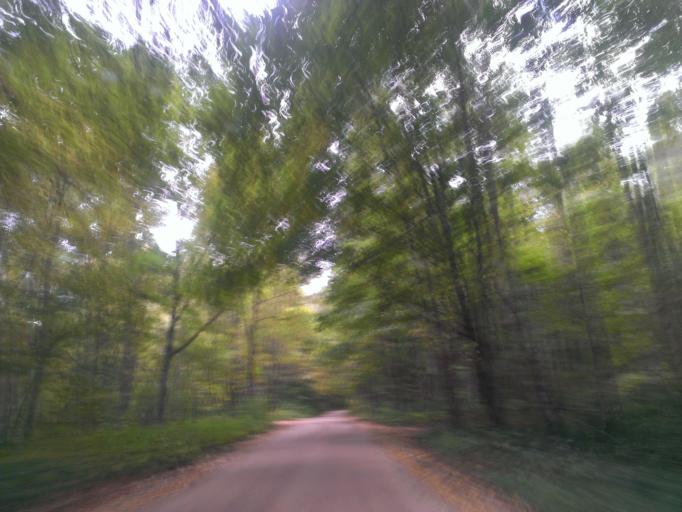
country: LV
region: Sigulda
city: Sigulda
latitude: 57.1515
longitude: 24.8321
